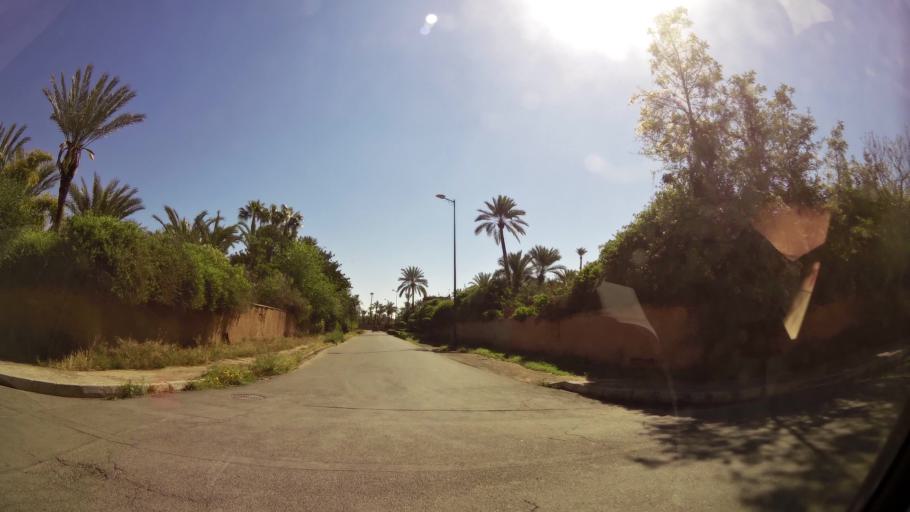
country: MA
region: Marrakech-Tensift-Al Haouz
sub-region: Marrakech
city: Marrakesh
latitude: 31.6472
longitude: -7.9771
